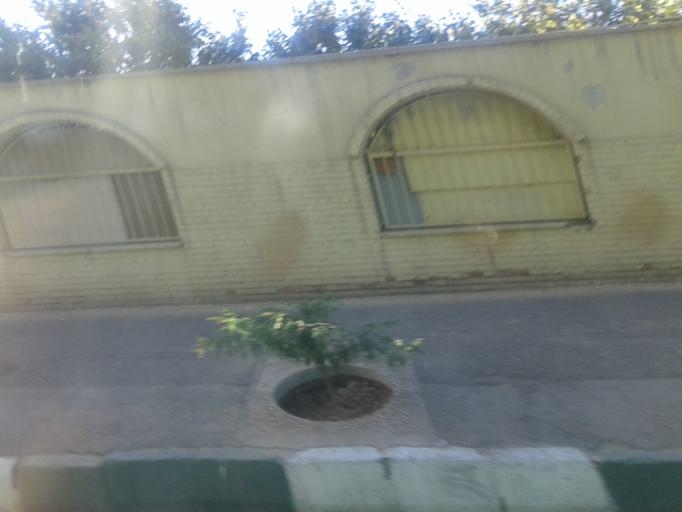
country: IR
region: Tehran
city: Tehran
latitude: 35.6319
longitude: 51.3632
